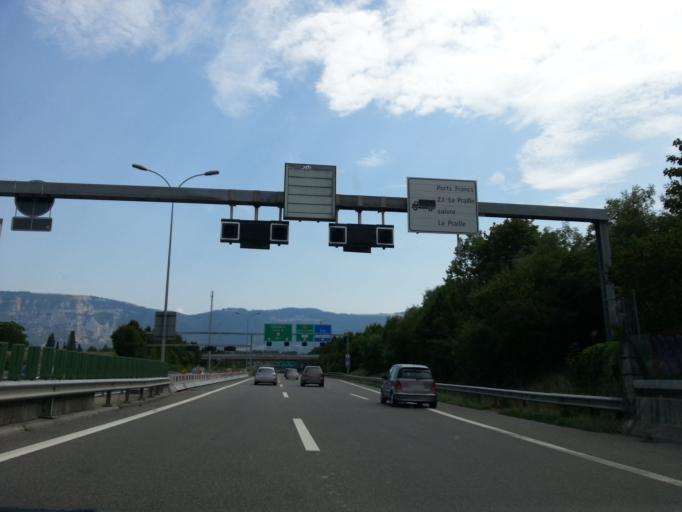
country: CH
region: Geneva
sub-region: Geneva
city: Confignon
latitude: 46.1714
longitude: 6.0920
